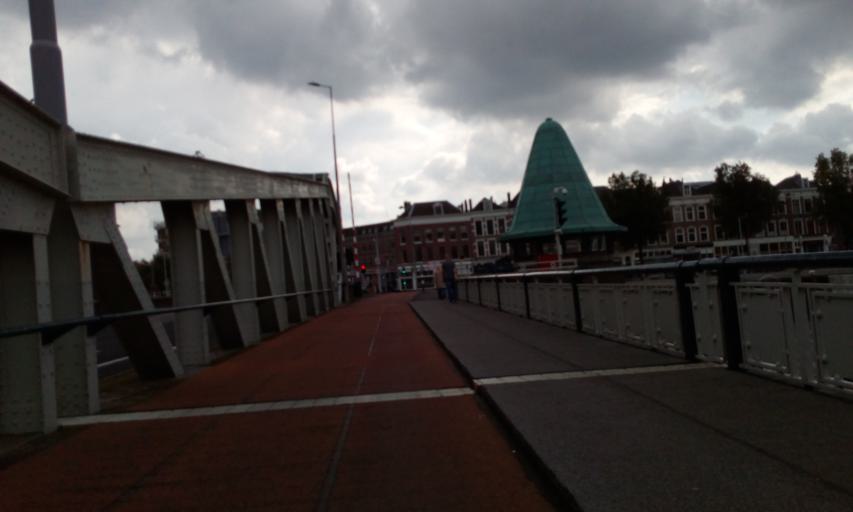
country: NL
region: South Holland
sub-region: Gemeente Rotterdam
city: Rotterdam
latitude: 51.9128
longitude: 4.4977
